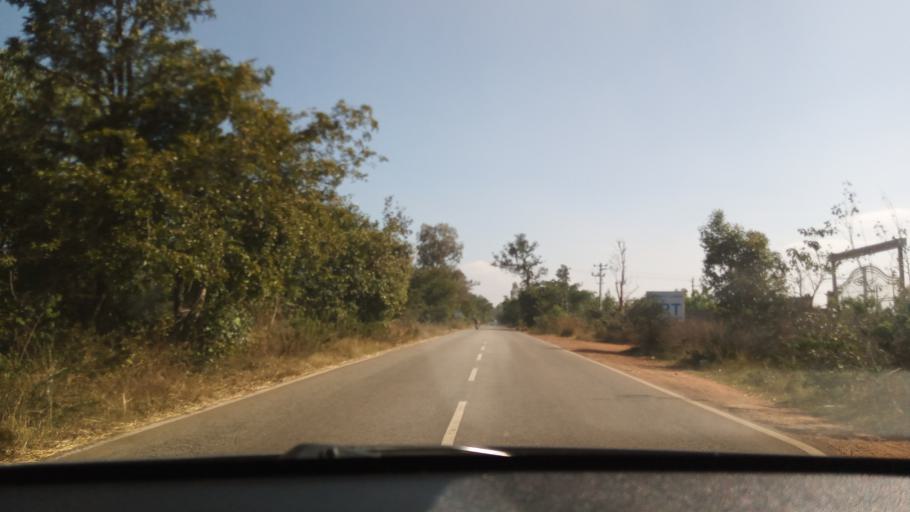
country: IN
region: Karnataka
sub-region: Bangalore Rural
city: Vijayapura
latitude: 13.2815
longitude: 77.7649
